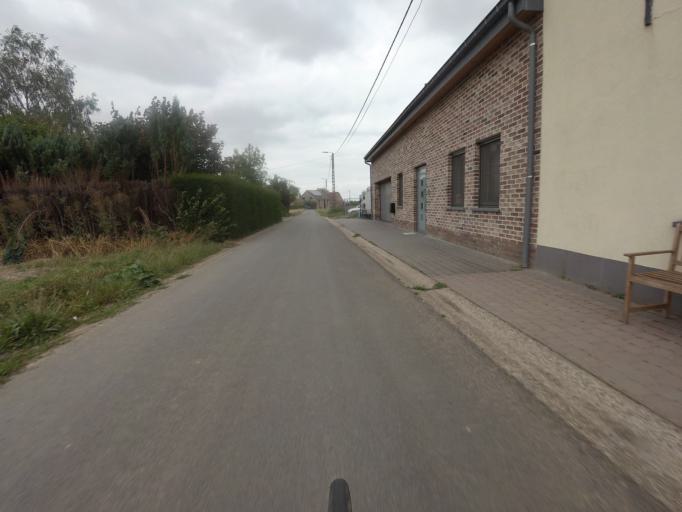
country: BE
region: Flanders
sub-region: Provincie Vlaams-Brabant
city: Herent
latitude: 50.9066
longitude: 4.6523
